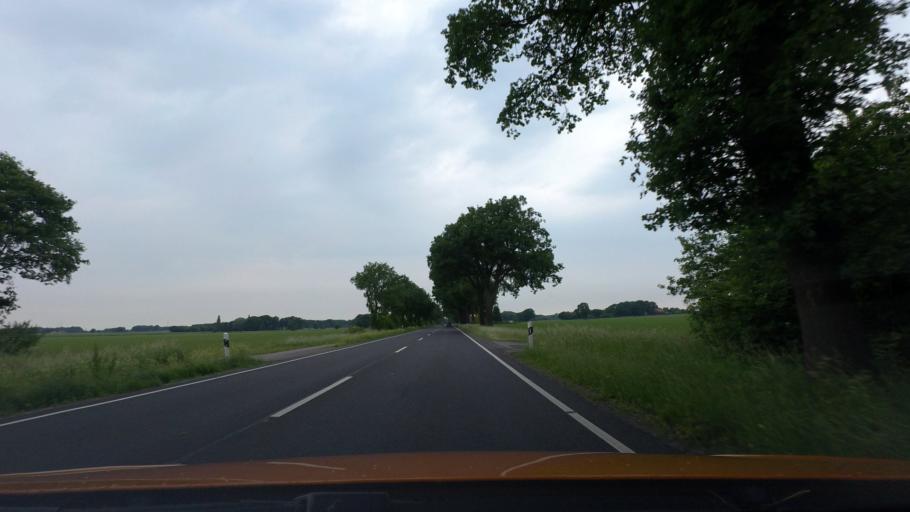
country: DE
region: Lower Saxony
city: Wietzen
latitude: 52.6928
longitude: 9.0913
